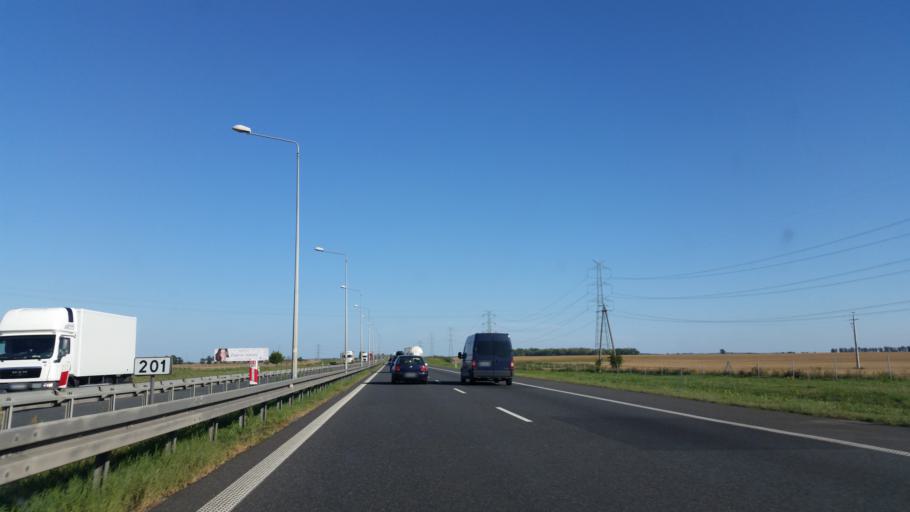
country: PL
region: Opole Voivodeship
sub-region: Powiat brzeski
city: Olszanka
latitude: 50.7544
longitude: 17.4348
